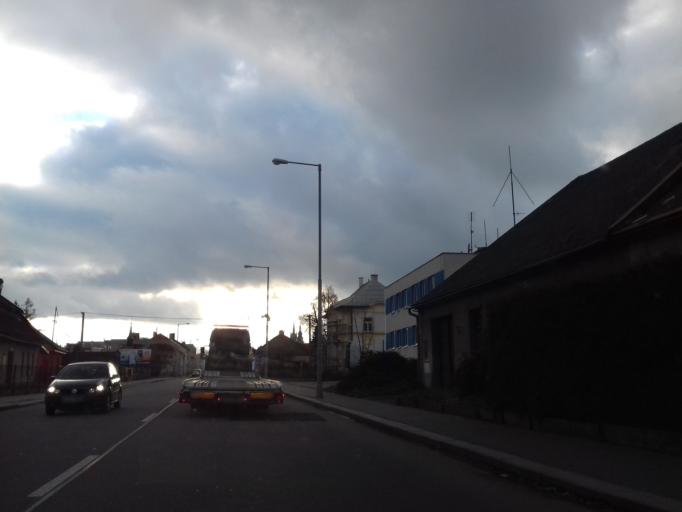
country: CZ
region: Pardubicky
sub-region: Okres Svitavy
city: Policka
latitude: 49.7176
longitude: 16.2732
